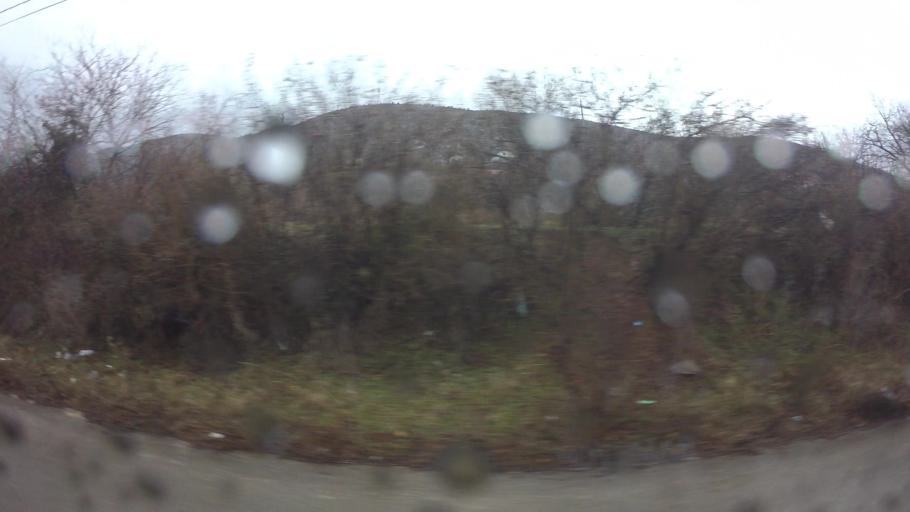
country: BA
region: Federation of Bosnia and Herzegovina
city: Blagaj
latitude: 43.2957
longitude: 17.8566
